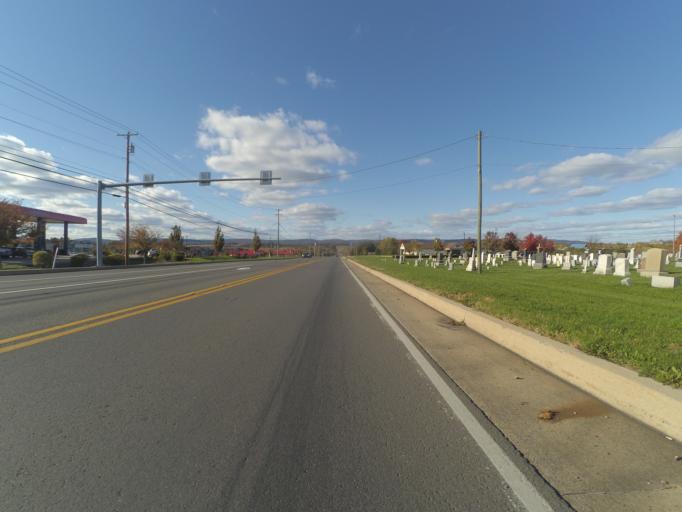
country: US
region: Pennsylvania
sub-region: Centre County
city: Houserville
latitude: 40.8363
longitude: -77.8013
